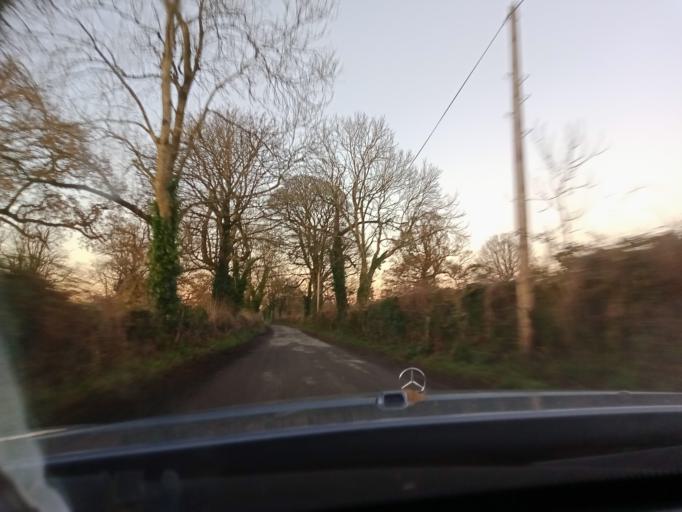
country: IE
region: Leinster
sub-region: Kilkenny
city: Thomastown
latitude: 52.4593
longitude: -7.1020
